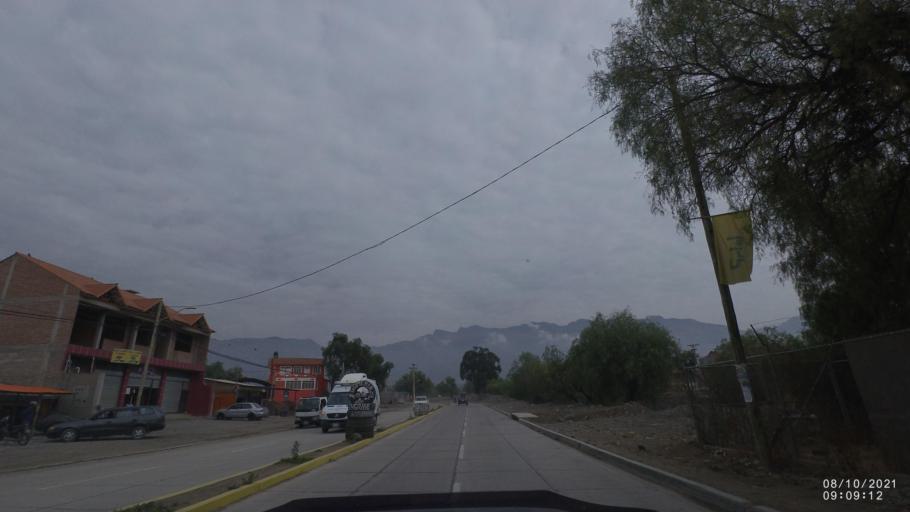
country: BO
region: Cochabamba
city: Sipe Sipe
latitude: -17.3972
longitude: -66.3266
